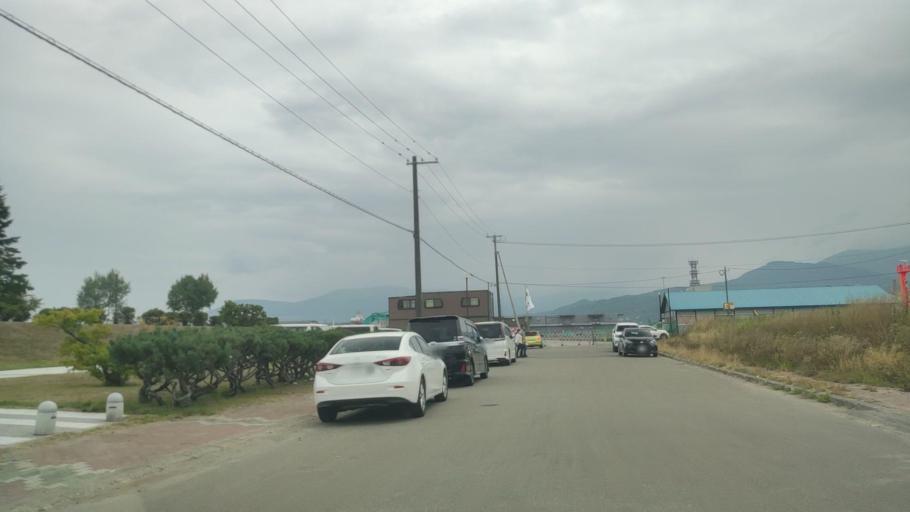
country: JP
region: Hokkaido
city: Otaru
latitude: 43.2046
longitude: 141.0025
